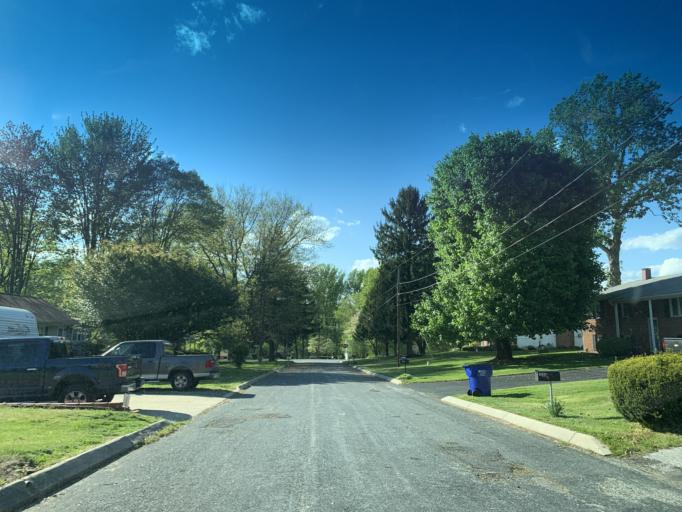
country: US
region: Maryland
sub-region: Harford County
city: Aberdeen
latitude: 39.5380
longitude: -76.2070
